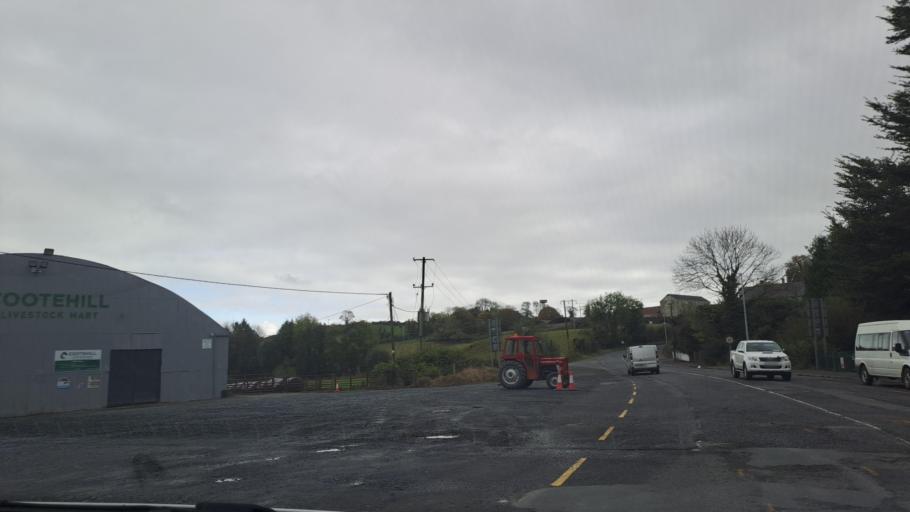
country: IE
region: Ulster
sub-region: An Cabhan
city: Cootehill
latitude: 54.0710
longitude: -7.0691
